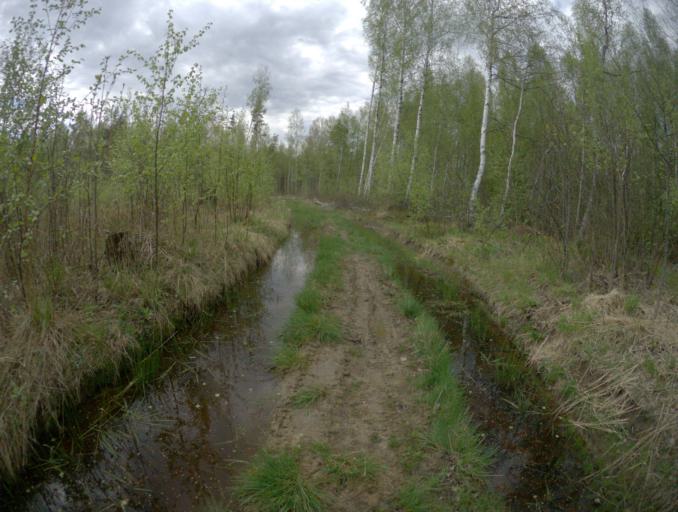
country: RU
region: Vladimir
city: Golovino
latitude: 55.9299
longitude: 40.3882
